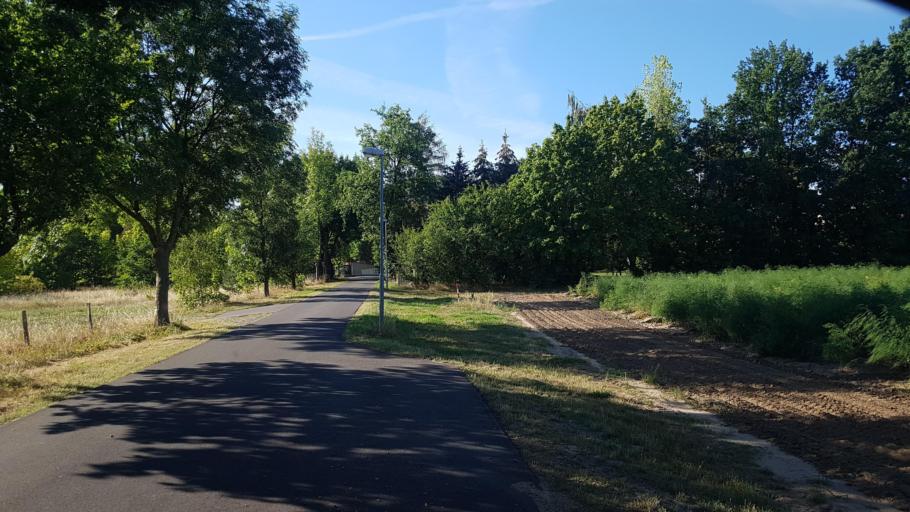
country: DE
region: Brandenburg
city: Golzow
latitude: 52.3067
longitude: 12.7187
